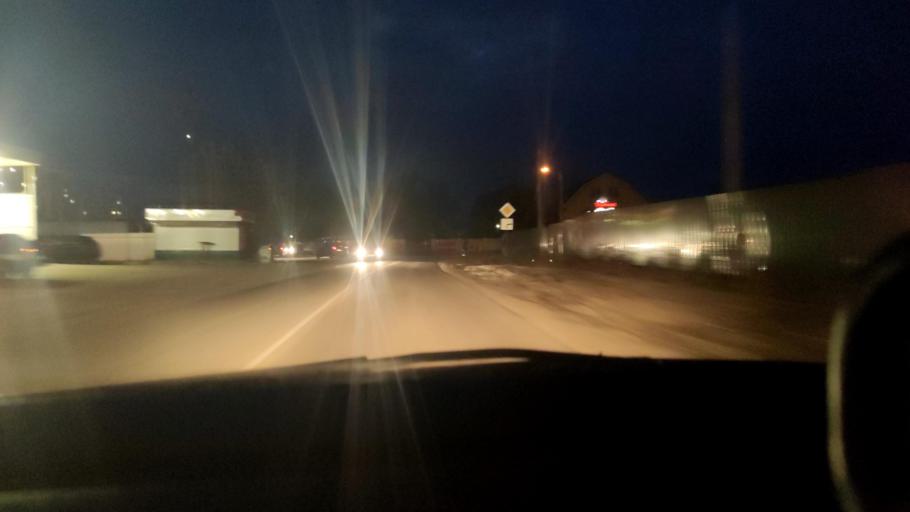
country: RU
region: Voronezj
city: Podgornoye
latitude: 51.7215
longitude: 39.1469
